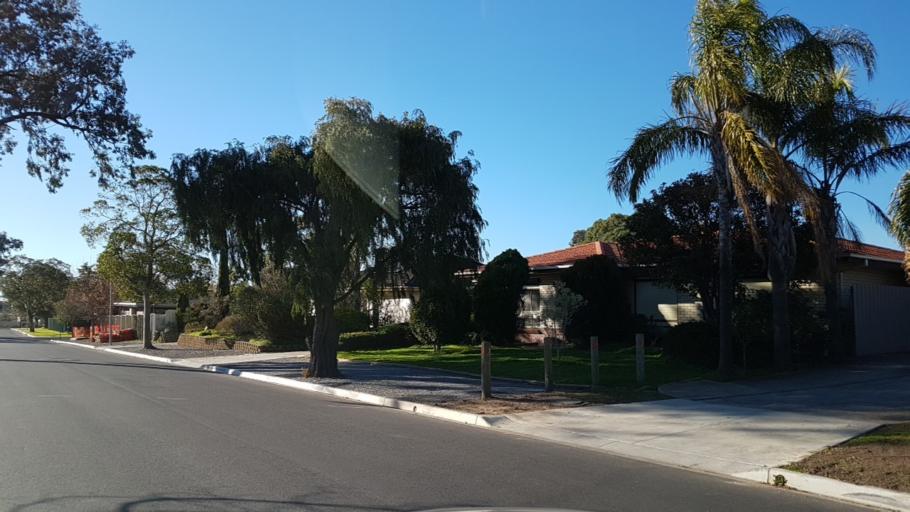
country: AU
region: South Australia
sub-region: Campbelltown
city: Campbelltown
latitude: -34.8843
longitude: 138.6833
